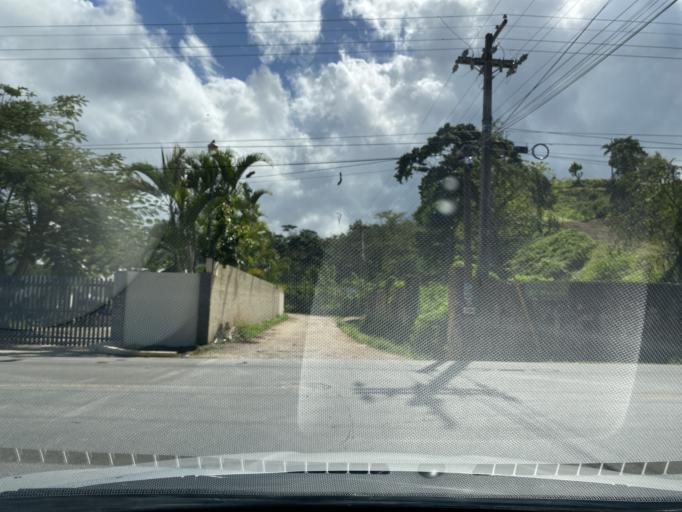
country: DO
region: Samana
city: Las Terrenas
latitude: 19.3112
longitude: -69.5286
